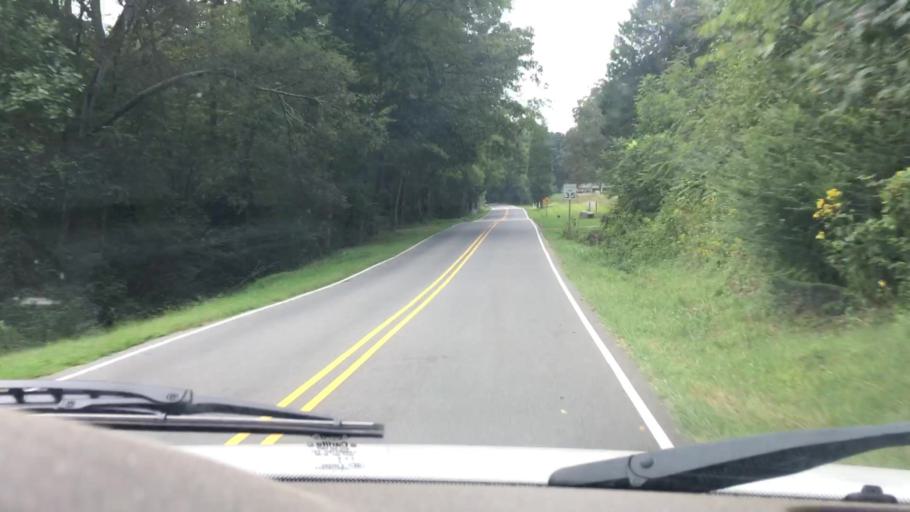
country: US
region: North Carolina
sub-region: Gaston County
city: Davidson
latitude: 35.4996
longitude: -80.8275
